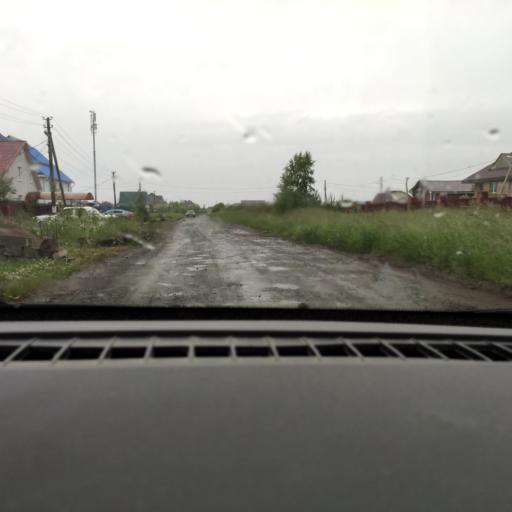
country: RU
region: Perm
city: Perm
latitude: 58.0401
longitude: 56.3726
